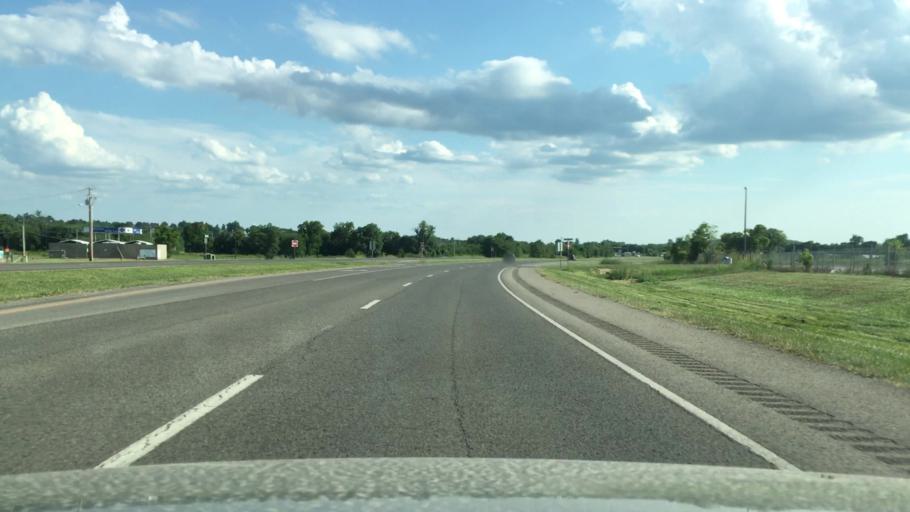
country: US
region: Oklahoma
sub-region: Cherokee County
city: Tahlequah
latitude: 35.9265
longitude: -95.0010
